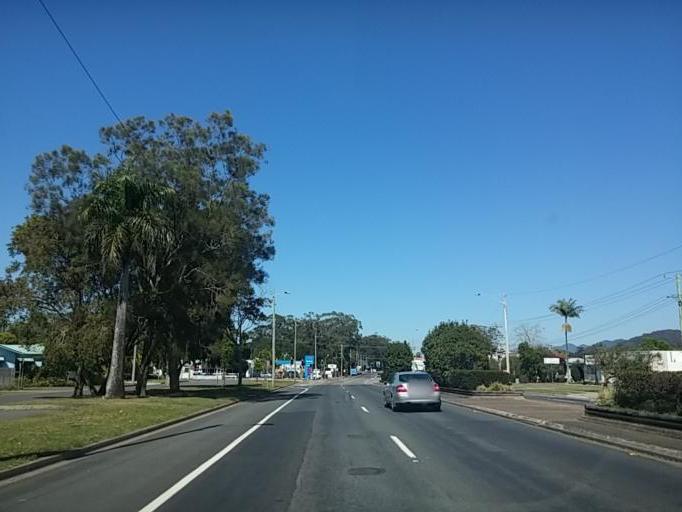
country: AU
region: New South Wales
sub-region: Coffs Harbour
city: Coffs Harbour
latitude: -30.2890
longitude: 153.1224
